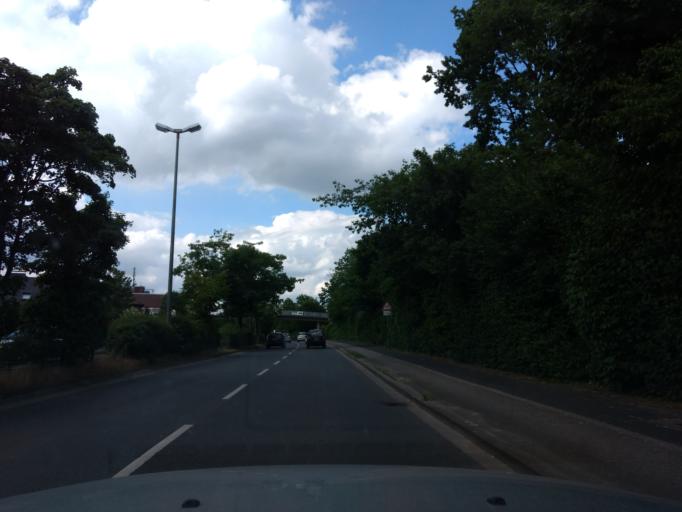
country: DE
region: North Rhine-Westphalia
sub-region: Regierungsbezirk Dusseldorf
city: Neuss
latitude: 51.1918
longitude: 6.6695
